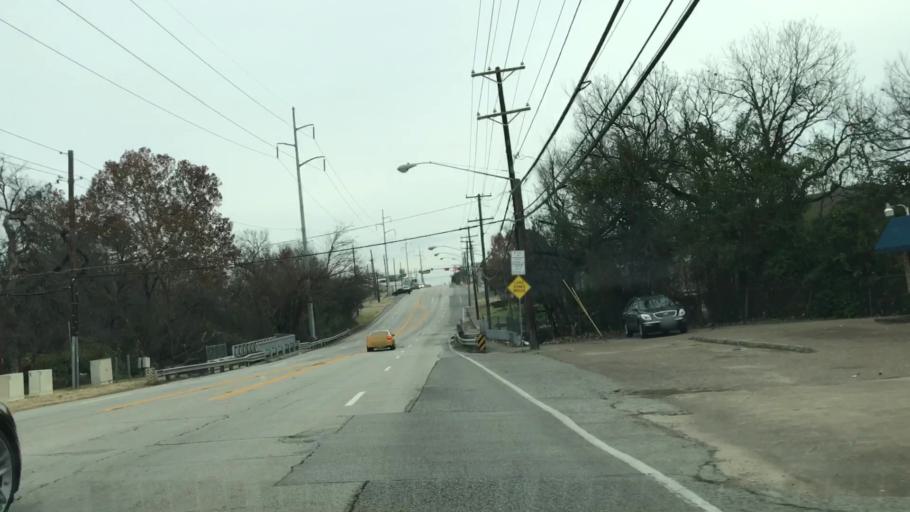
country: US
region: Texas
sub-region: Dallas County
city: Cockrell Hill
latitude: 32.7495
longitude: -96.8652
